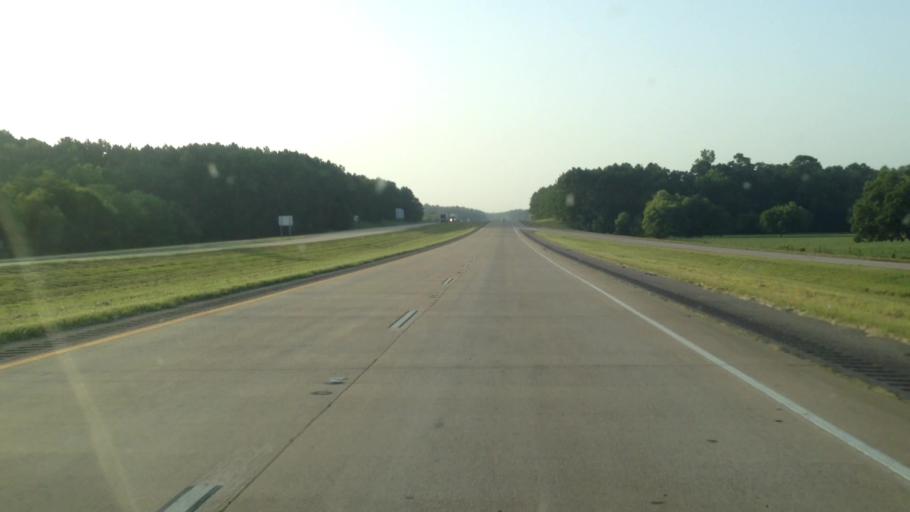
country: US
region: Louisiana
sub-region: Grant Parish
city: Colfax
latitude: 31.4923
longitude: -92.8589
